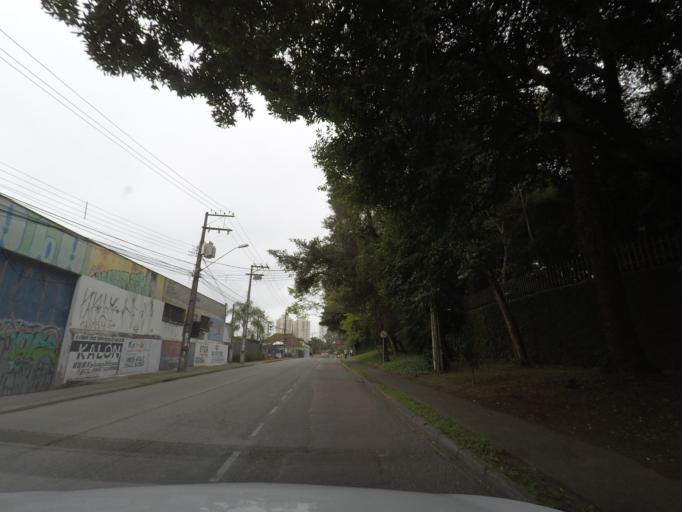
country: BR
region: Parana
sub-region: Curitiba
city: Curitiba
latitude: -25.4504
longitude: -49.3511
